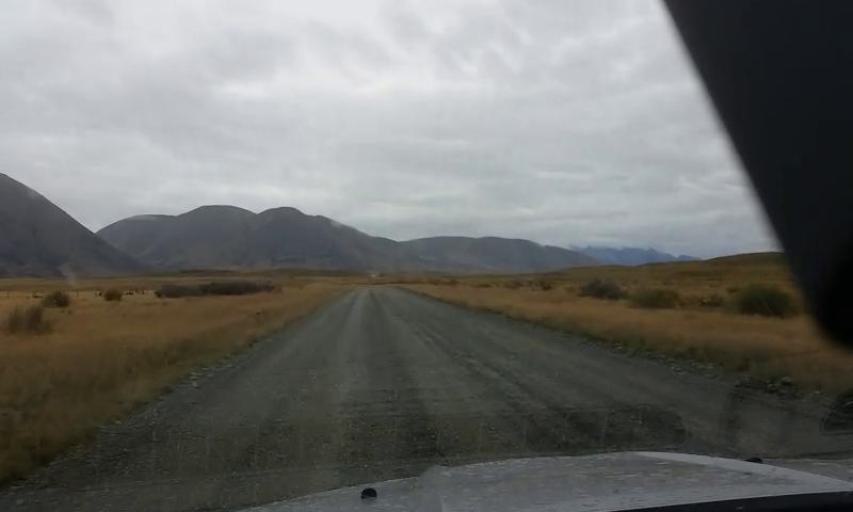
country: NZ
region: Canterbury
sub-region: Ashburton District
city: Methven
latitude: -43.6147
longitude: 171.1100
